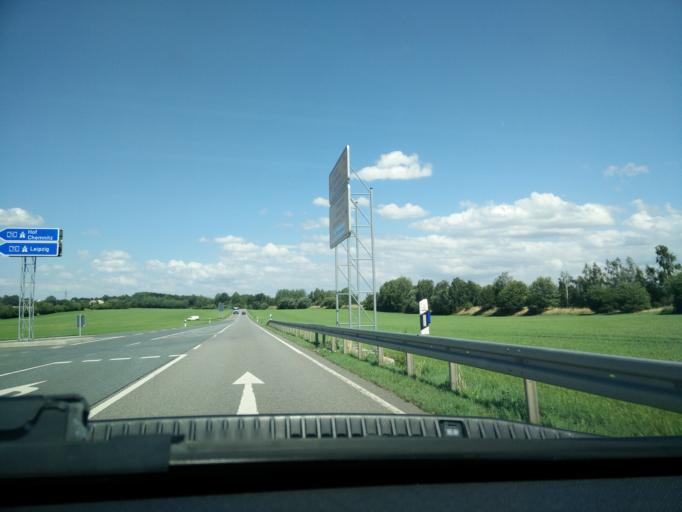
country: DE
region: Saxony
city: Narsdorf
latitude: 50.9959
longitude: 12.7033
